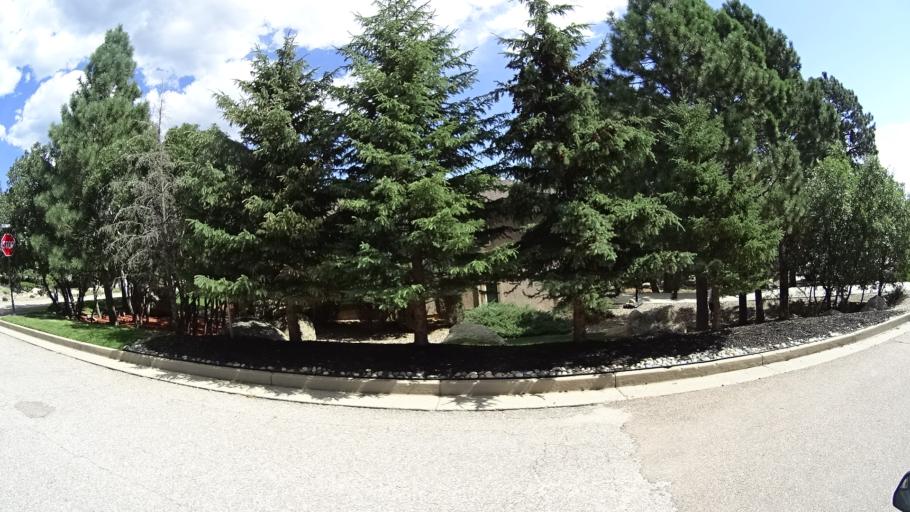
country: US
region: Colorado
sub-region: El Paso County
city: Fort Carson
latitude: 38.7512
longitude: -104.8391
